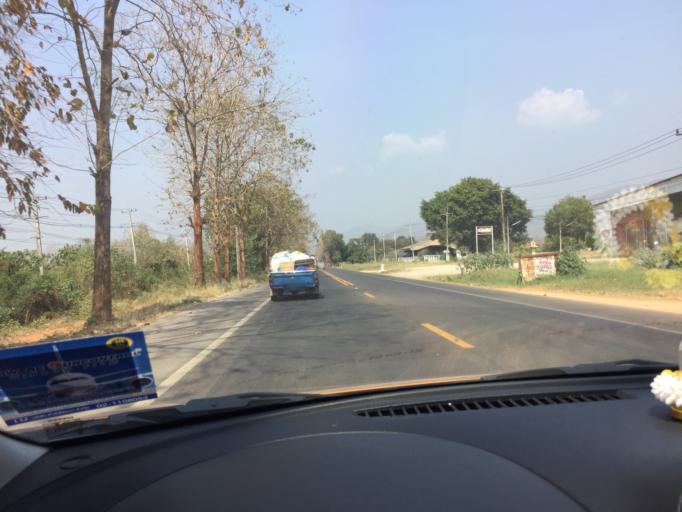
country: TH
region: Kanchanaburi
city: Sai Yok
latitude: 14.1732
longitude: 99.1296
